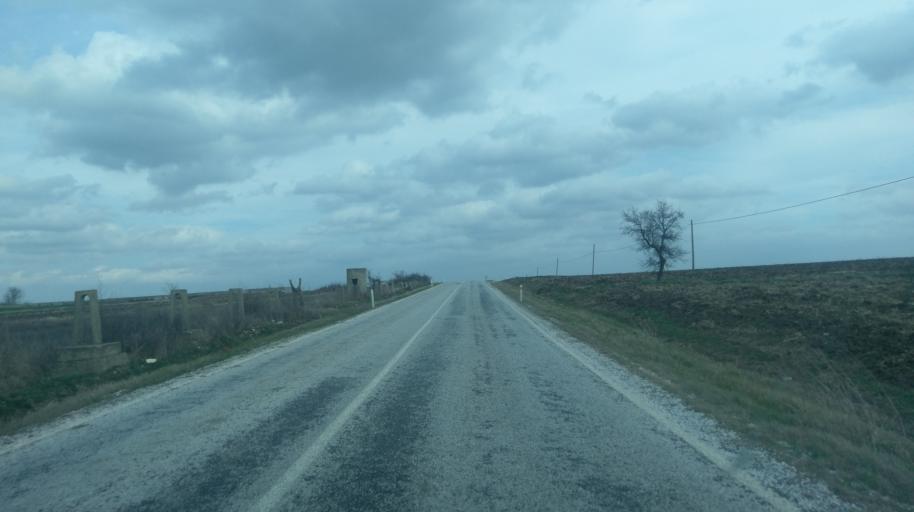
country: TR
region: Edirne
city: Haskoy
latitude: 41.6636
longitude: 26.9453
